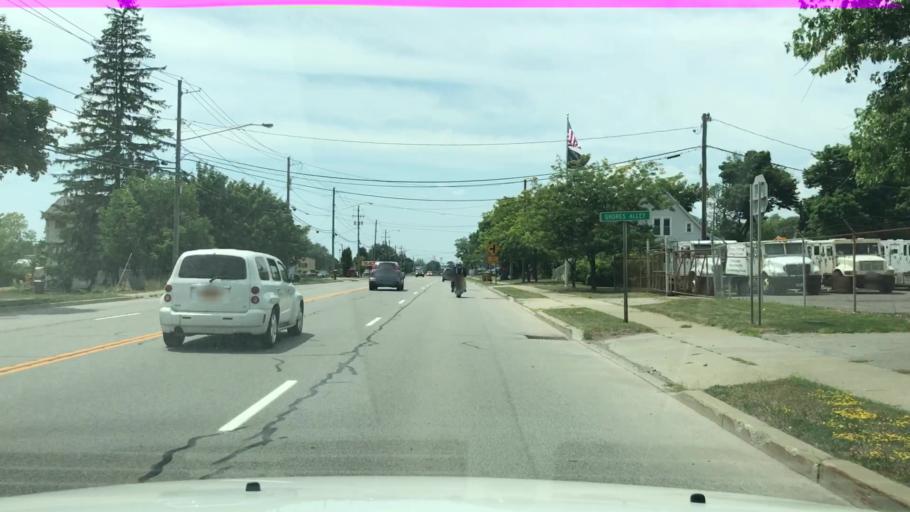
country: US
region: New York
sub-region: Erie County
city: Cheektowaga
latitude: 42.9039
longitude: -78.7474
